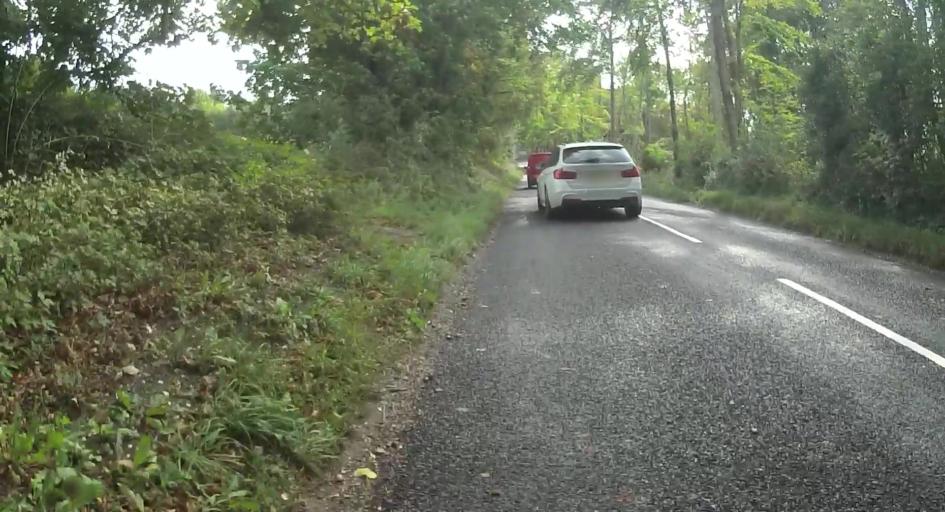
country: GB
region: England
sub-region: Hampshire
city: Kings Worthy
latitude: 51.0758
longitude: -1.1729
